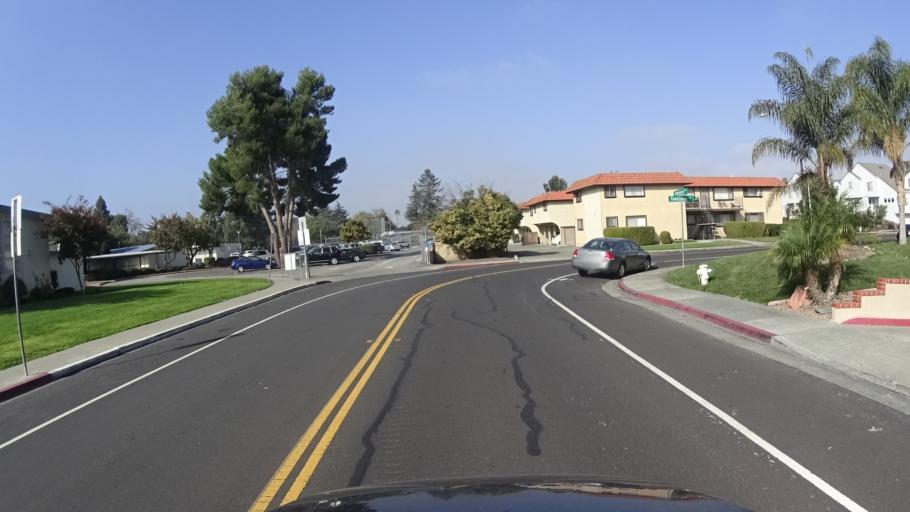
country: US
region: California
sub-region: Santa Clara County
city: Santa Clara
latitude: 37.3580
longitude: -121.9868
